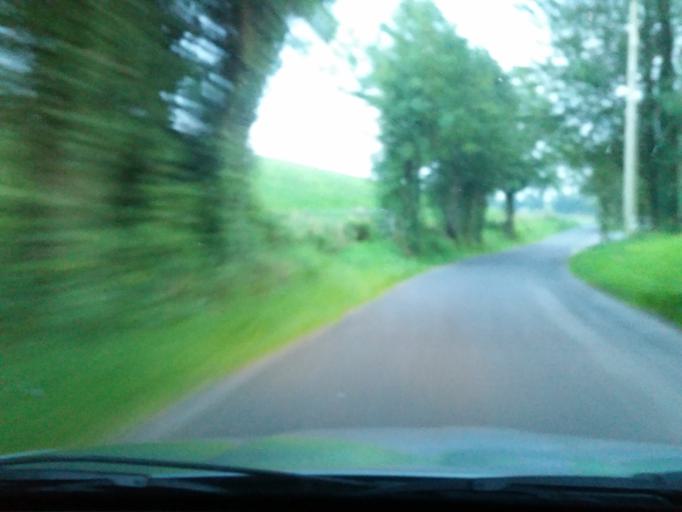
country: IE
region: Ulster
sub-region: County Monaghan
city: Clones
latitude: 54.2455
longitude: -7.2657
